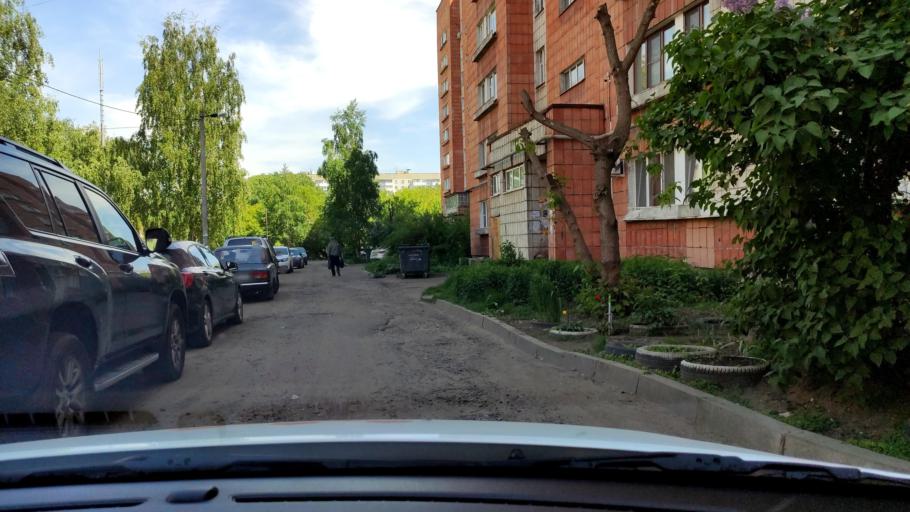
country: RU
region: Tatarstan
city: Osinovo
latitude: 55.8189
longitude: 48.8880
